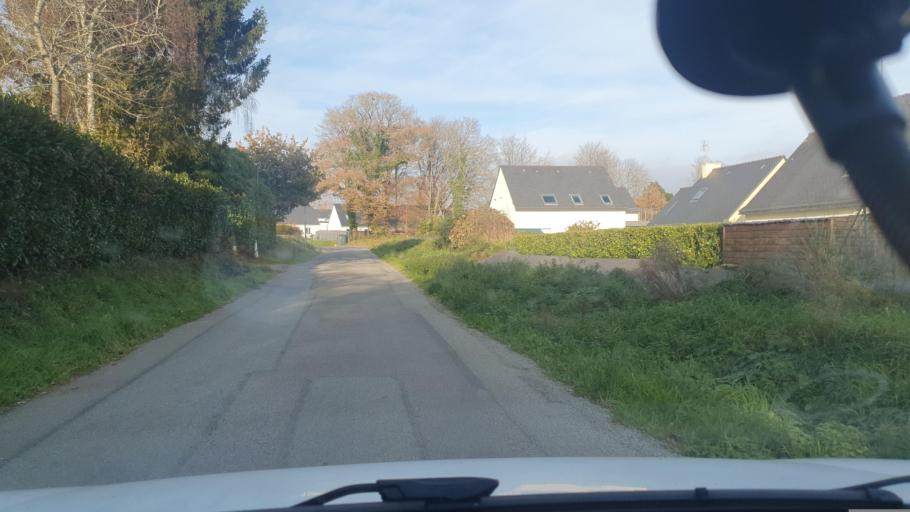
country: FR
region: Brittany
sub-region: Departement du Finistere
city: Briec
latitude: 48.0988
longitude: -4.0087
